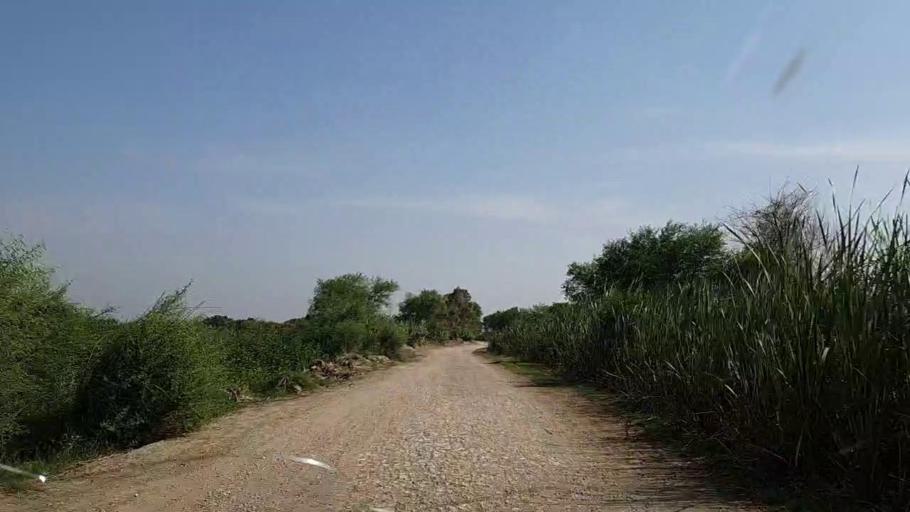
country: PK
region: Sindh
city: Khanpur
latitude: 27.7239
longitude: 69.3604
